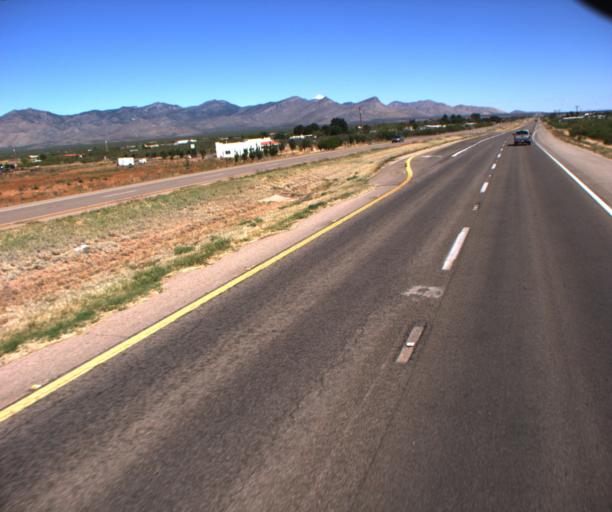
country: US
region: Arizona
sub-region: Cochise County
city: Huachuca City
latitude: 31.6998
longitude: -110.3502
